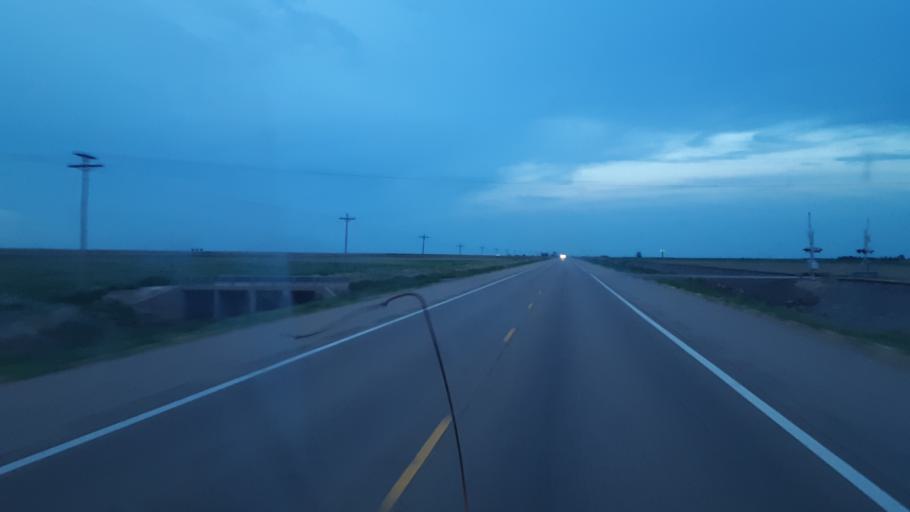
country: US
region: Kansas
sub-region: Hamilton County
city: Syracuse
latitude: 37.9655
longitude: -101.6892
